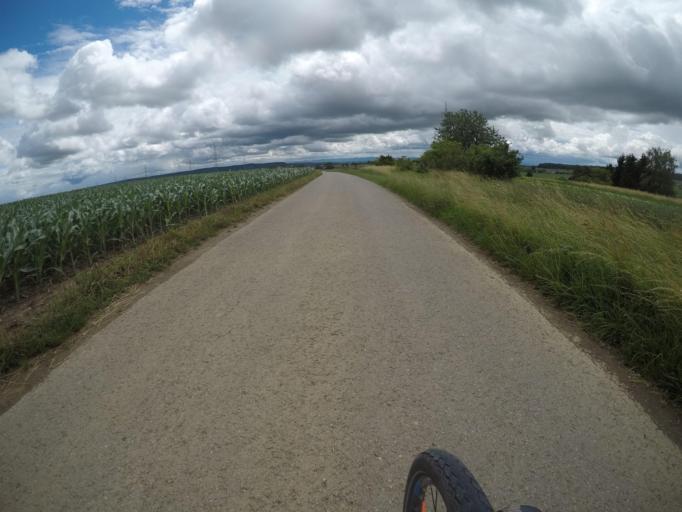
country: DE
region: Baden-Wuerttemberg
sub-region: Regierungsbezirk Stuttgart
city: Deckenpfronn
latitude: 48.6178
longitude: 8.8227
